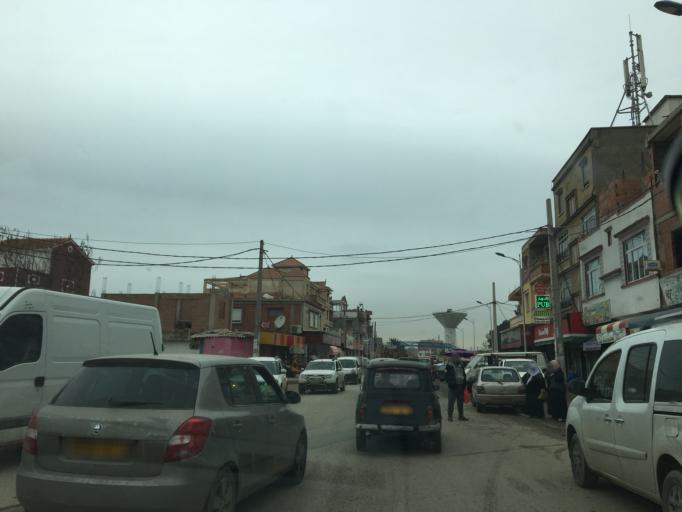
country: DZ
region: Alger
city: Rouiba
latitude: 36.7575
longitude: 3.2494
